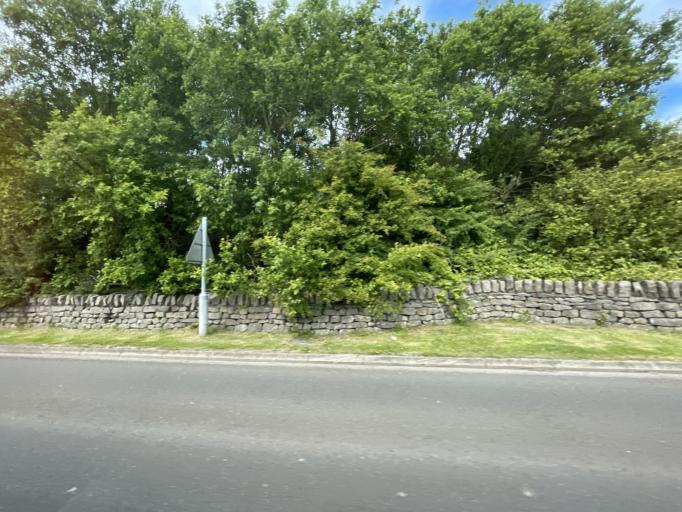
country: GB
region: Wales
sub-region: Anglesey
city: Llanfairpwllgwyngyll
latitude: 53.2221
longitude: -4.2184
